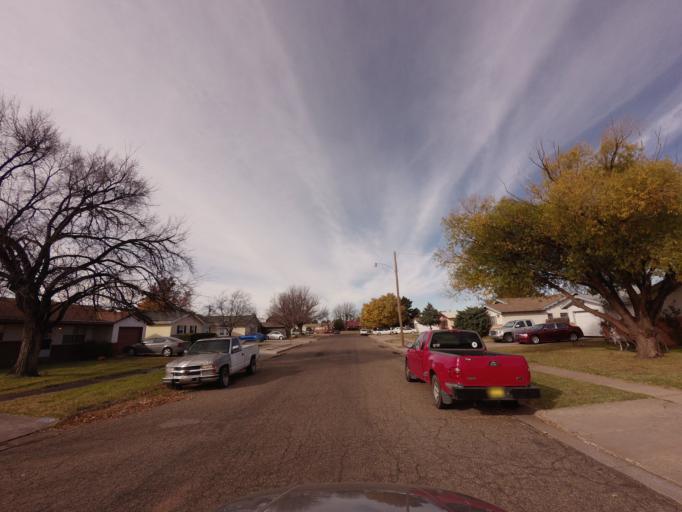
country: US
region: New Mexico
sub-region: Curry County
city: Clovis
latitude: 34.4254
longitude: -103.2158
